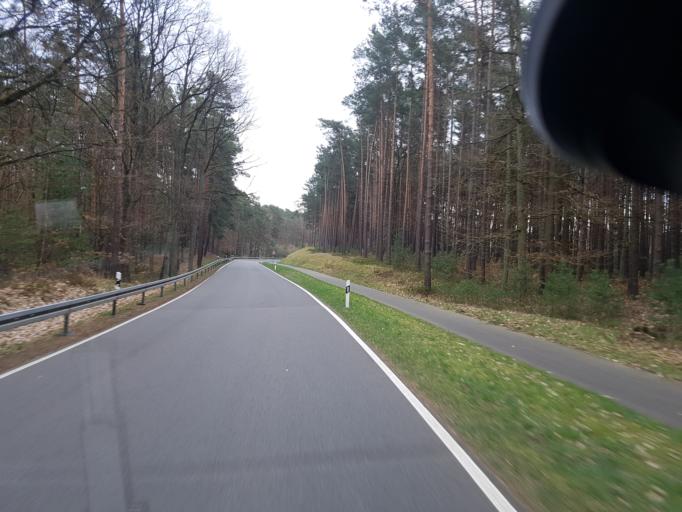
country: DE
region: Brandenburg
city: Gross Lindow
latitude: 52.1590
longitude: 14.5084
